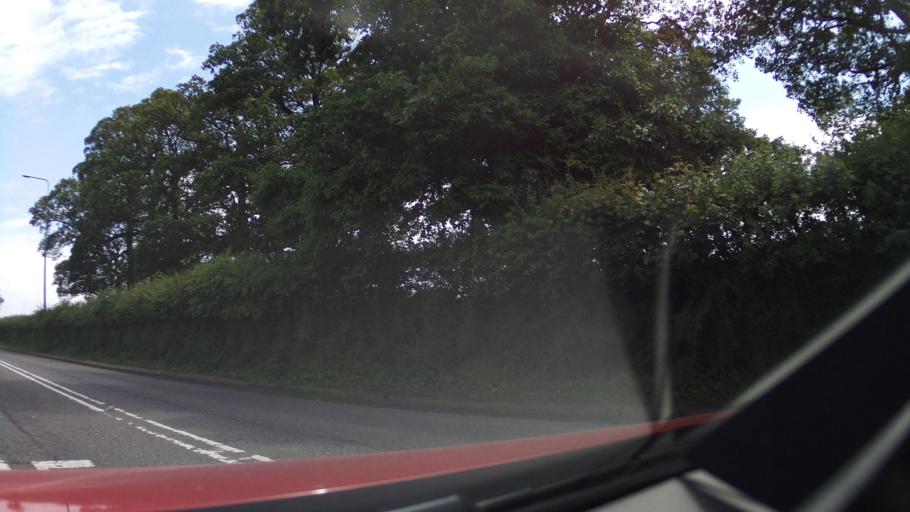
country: GB
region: Wales
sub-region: Vale of Glamorgan
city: Penllyn
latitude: 51.4681
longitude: -3.4752
